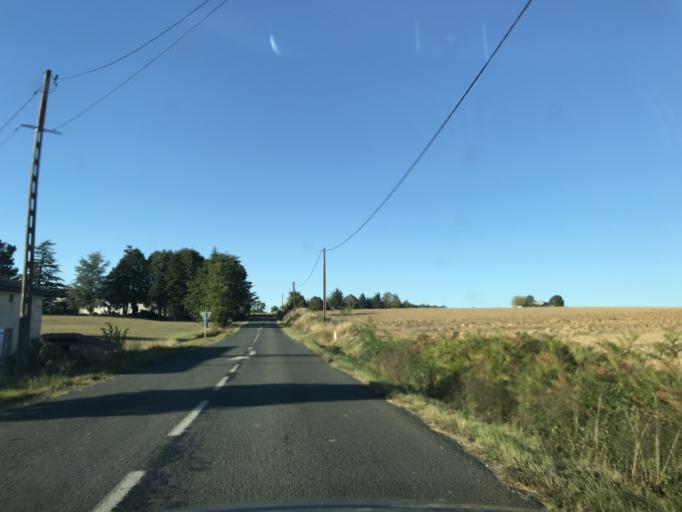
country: FR
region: Aquitaine
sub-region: Departement de la Gironde
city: Sauveterre-de-Guyenne
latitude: 44.7079
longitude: -0.0668
